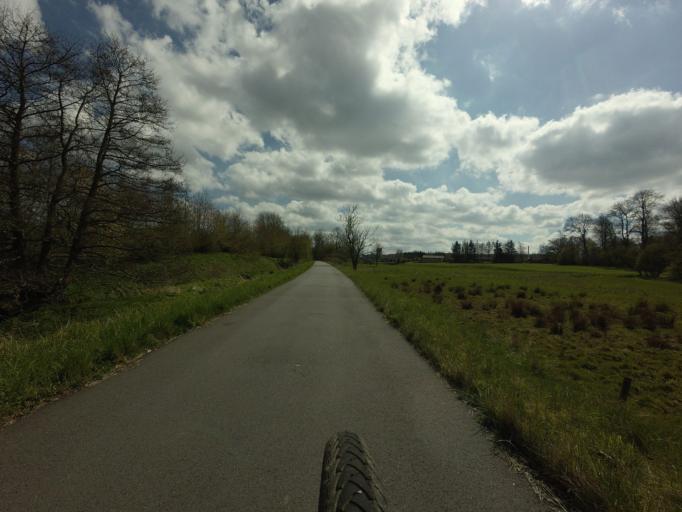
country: DK
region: North Denmark
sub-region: Mariagerfjord Kommune
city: Hadsund
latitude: 56.8355
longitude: 10.1164
